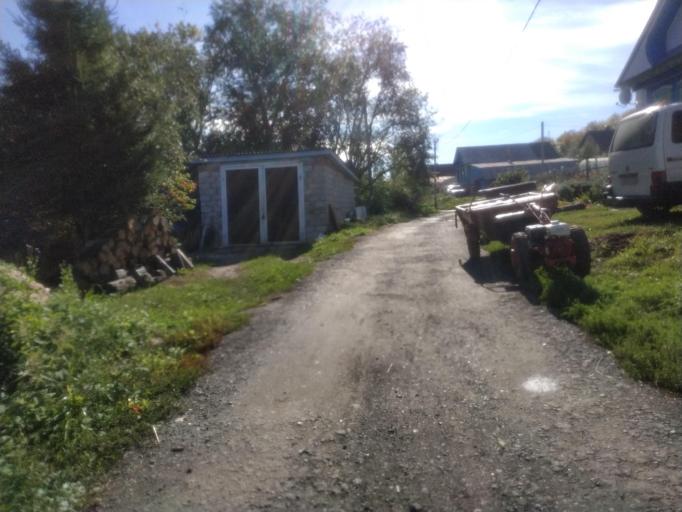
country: RU
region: Chuvashia
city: Novyye Lapsary
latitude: 56.1475
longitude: 47.1514
